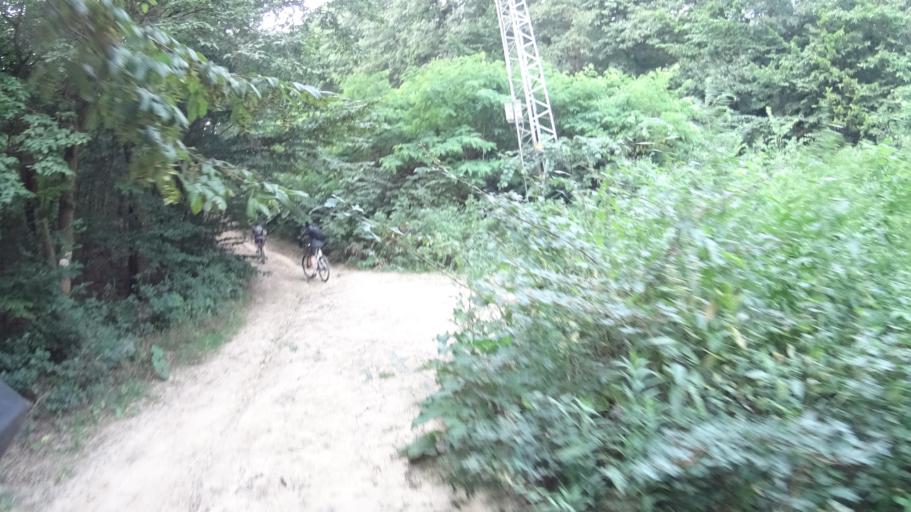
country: HU
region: Pest
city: Budakeszi
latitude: 47.4928
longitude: 18.9367
